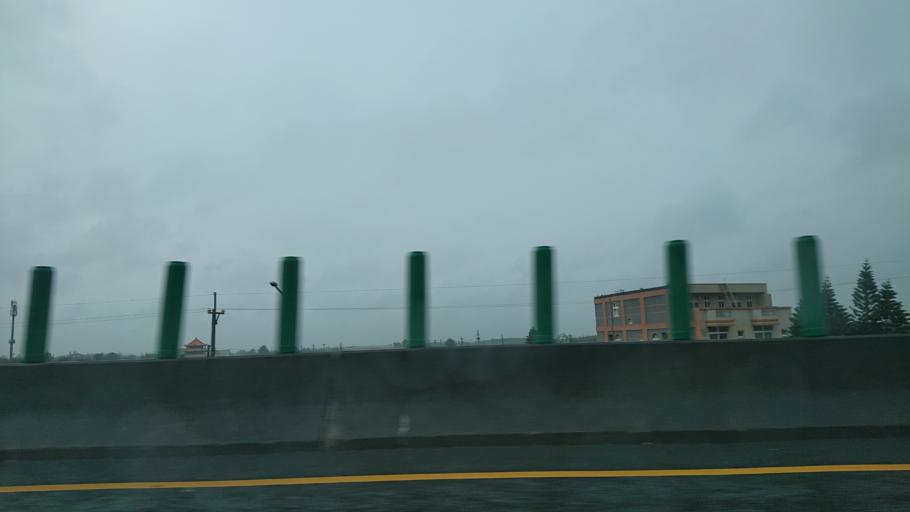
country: TW
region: Taiwan
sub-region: Chiayi
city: Taibao
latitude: 23.7226
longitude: 120.2169
